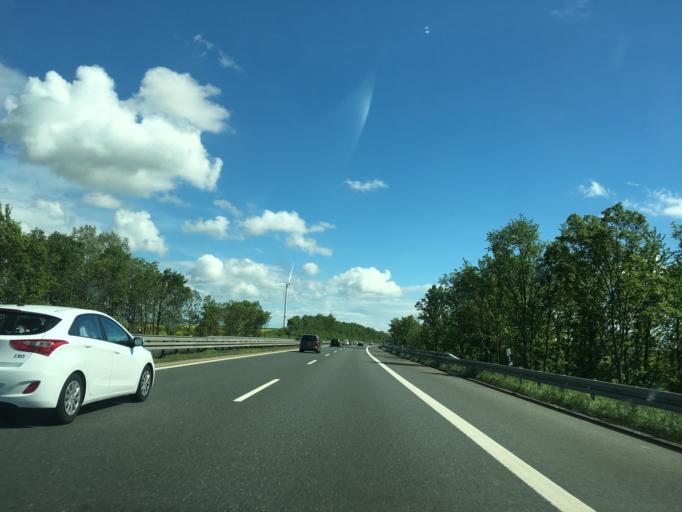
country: DE
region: Bavaria
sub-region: Regierungsbezirk Unterfranken
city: Wasserlosen
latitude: 50.0463
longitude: 10.0610
